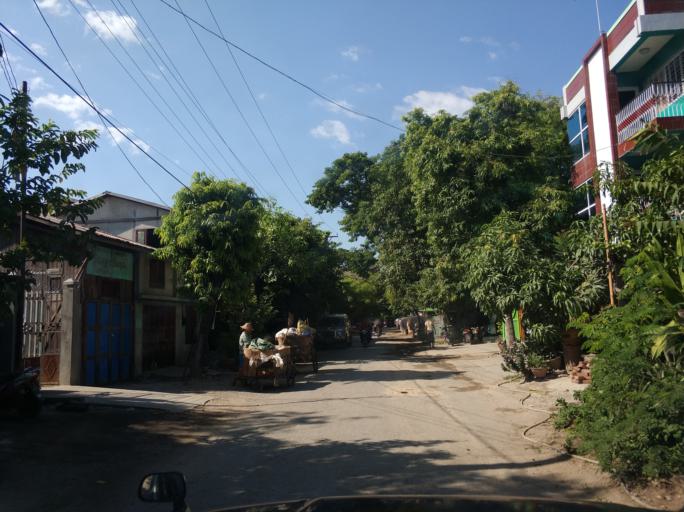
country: MM
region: Mandalay
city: Mandalay
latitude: 21.9716
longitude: 96.0688
